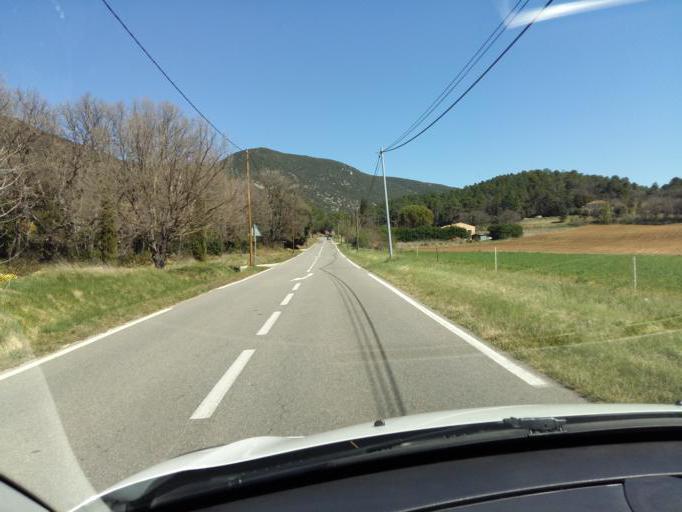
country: FR
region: Provence-Alpes-Cote d'Azur
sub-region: Departement du Vaucluse
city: Saignon
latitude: 43.9174
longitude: 5.4736
